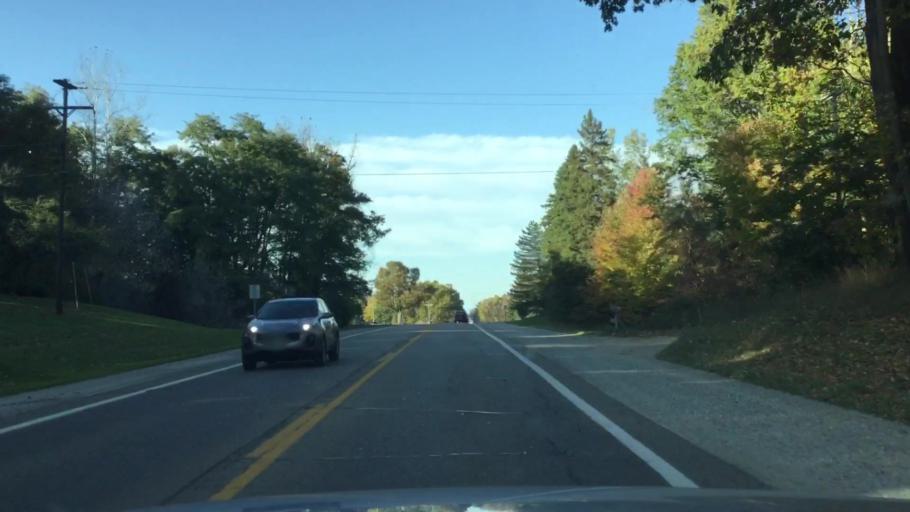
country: US
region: Michigan
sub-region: Lapeer County
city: Barnes Lake-Millers Lake
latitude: 43.1343
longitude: -83.3106
